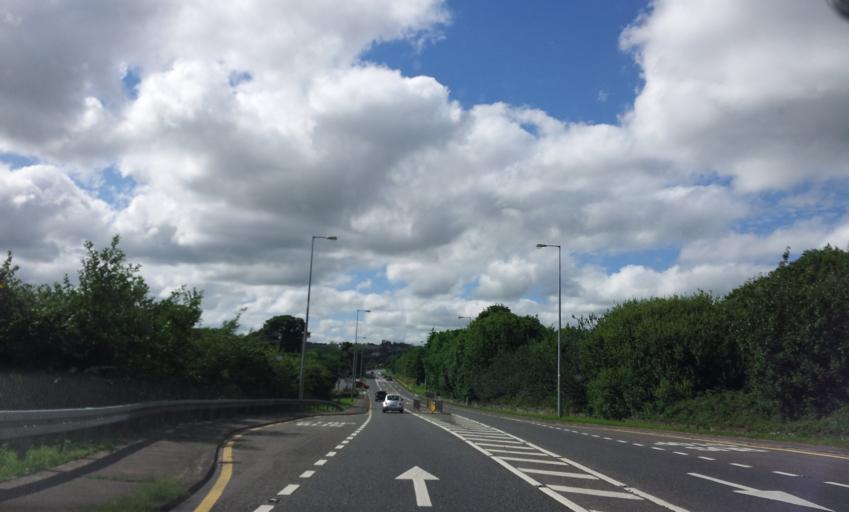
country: IE
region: Munster
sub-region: County Cork
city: Killumney
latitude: 51.8800
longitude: -8.6522
